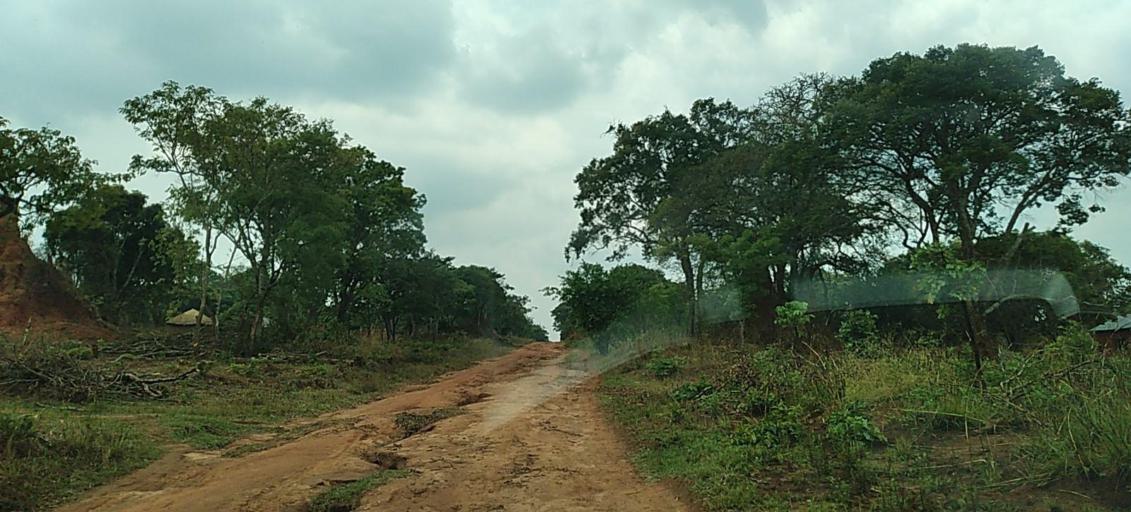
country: ZM
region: North-Western
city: Mwinilunga
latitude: -11.5348
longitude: 24.7837
